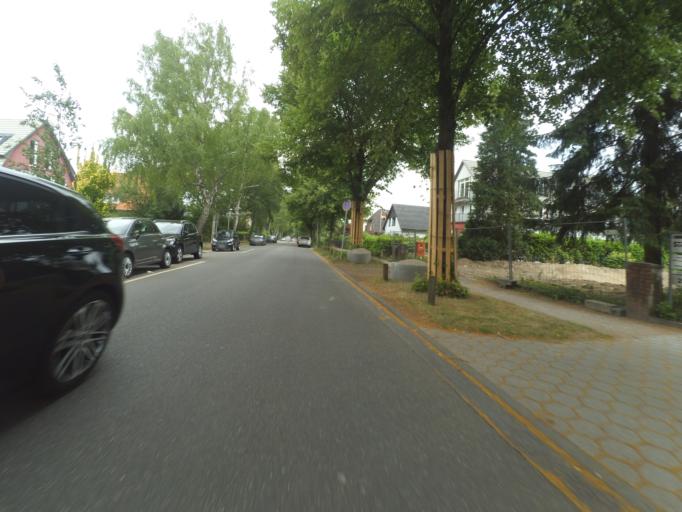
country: DE
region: Hamburg
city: Poppenbuettel
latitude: 53.6533
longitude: 10.0965
